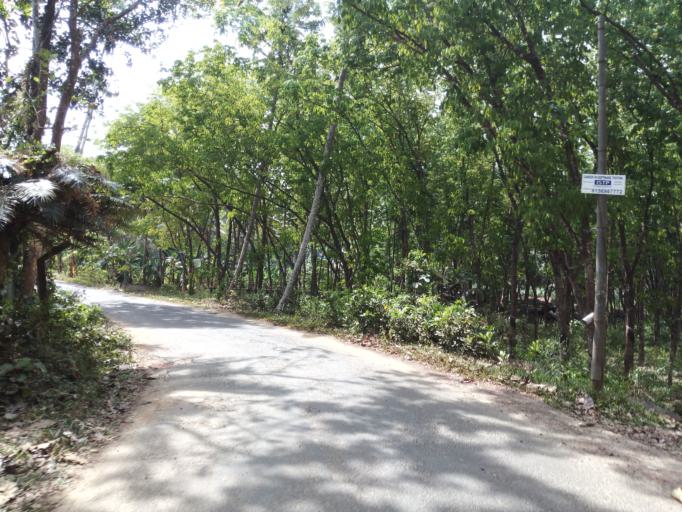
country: IN
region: Kerala
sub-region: Kottayam
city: Palackattumala
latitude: 9.8696
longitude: 76.6469
